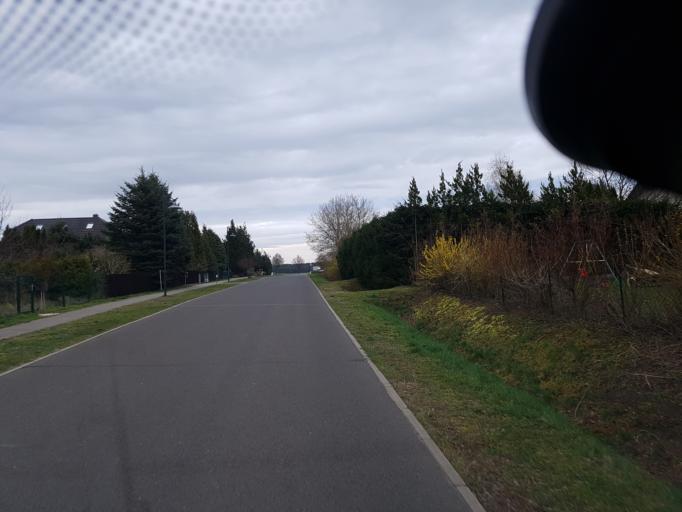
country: DE
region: Brandenburg
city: Mixdorf
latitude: 52.1983
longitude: 14.4037
